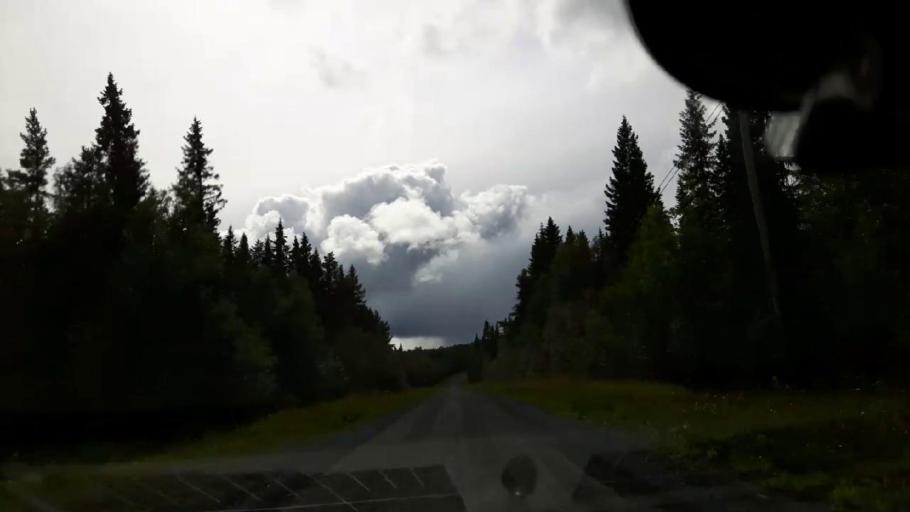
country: SE
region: Jaemtland
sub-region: Krokoms Kommun
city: Valla
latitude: 63.3594
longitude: 13.8574
